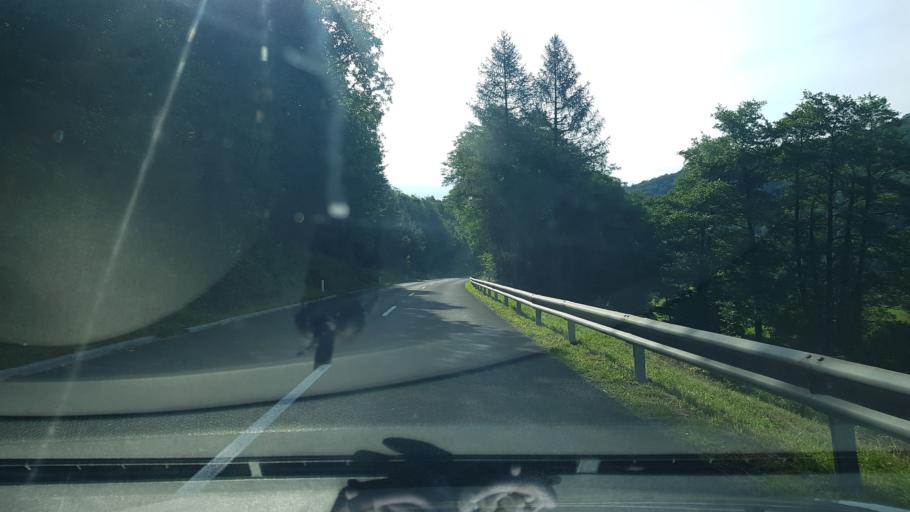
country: SI
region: Divaca
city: Divaca
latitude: 45.6566
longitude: 14.0591
